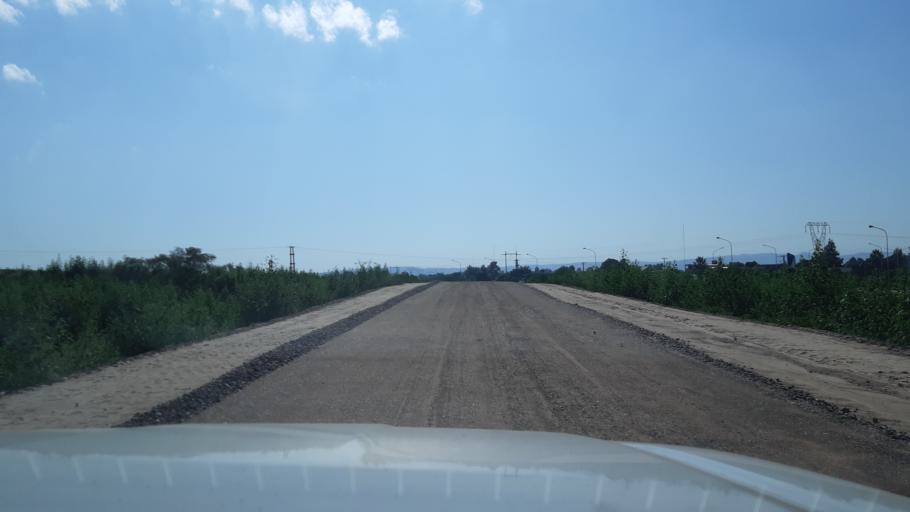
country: AR
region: Salta
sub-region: Departamento de General Guemes
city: General Martin Miguel de Guemes
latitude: -24.5317
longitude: -65.0786
